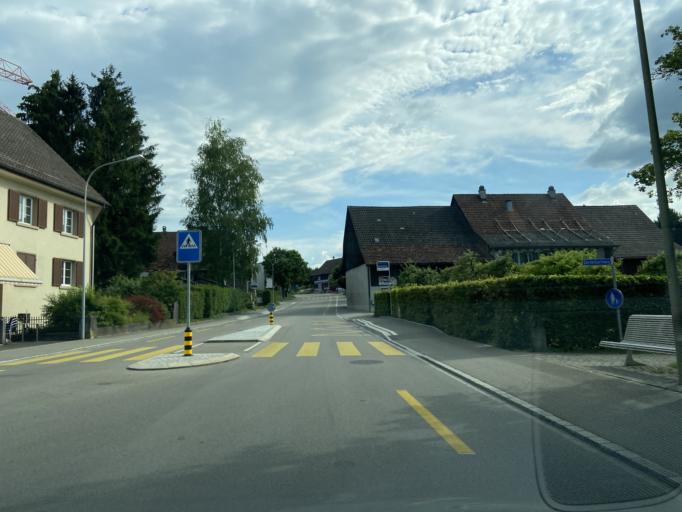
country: CH
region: Zurich
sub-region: Bezirk Winterthur
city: Seuzach Dorf
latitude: 47.5356
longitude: 8.7297
